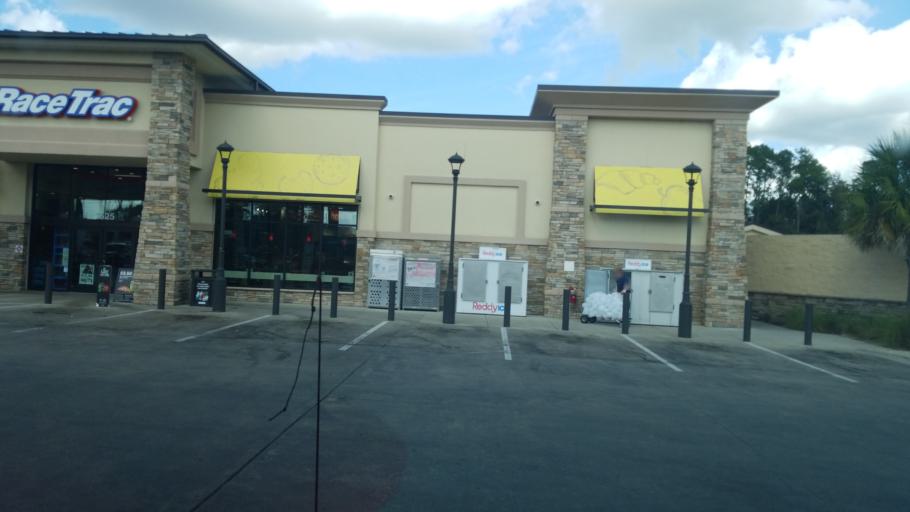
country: US
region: Florida
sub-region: Marion County
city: Belleview
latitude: 29.0262
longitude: -82.1521
